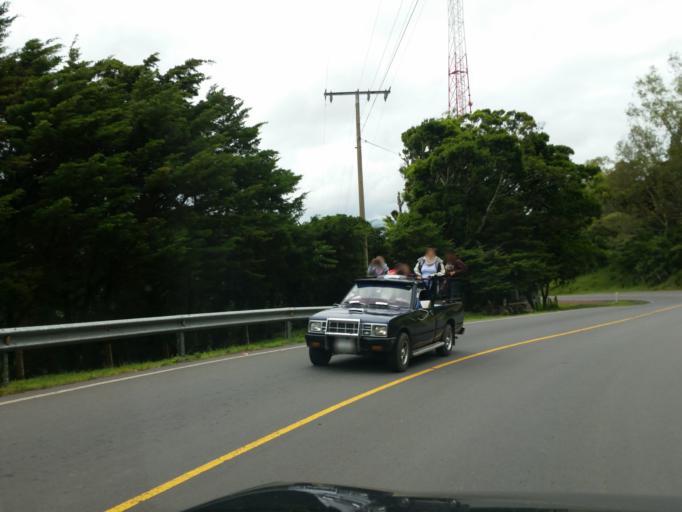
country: NI
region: Matagalpa
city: Matagalpa
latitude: 12.9822
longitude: -85.9210
